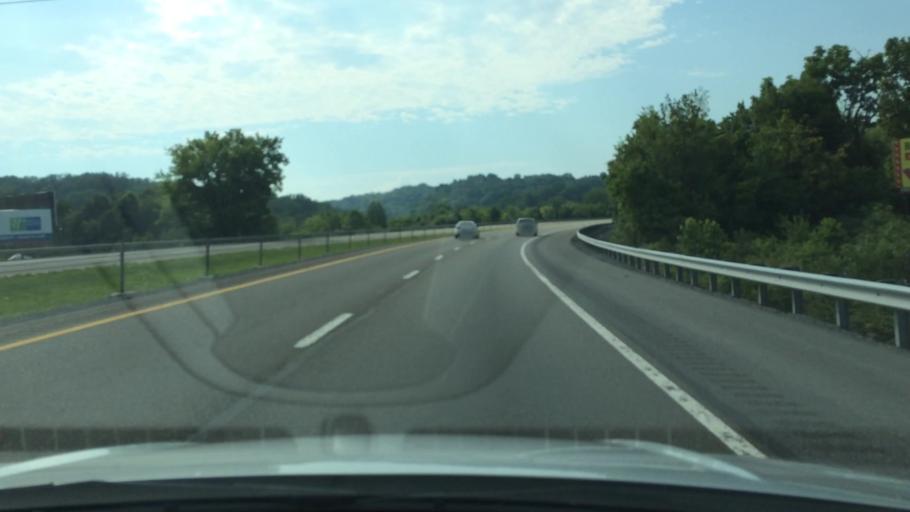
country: US
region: Tennessee
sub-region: Cocke County
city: Newport
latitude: 35.9820
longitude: -83.2759
